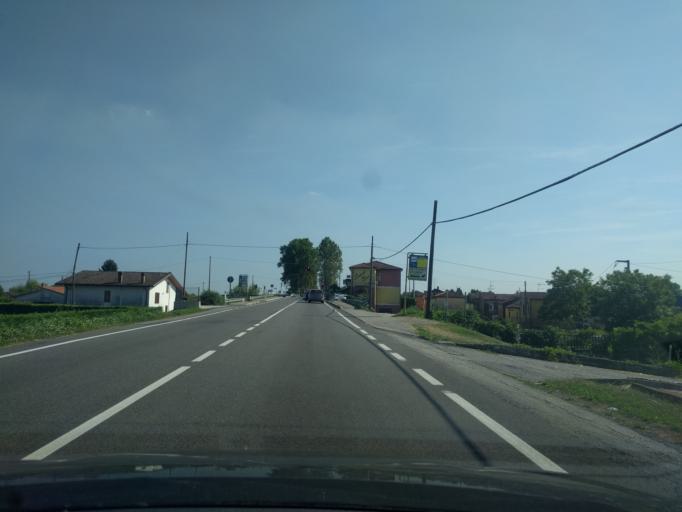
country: IT
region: Veneto
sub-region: Provincia di Padova
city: Stanghella
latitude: 45.1466
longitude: 11.7570
